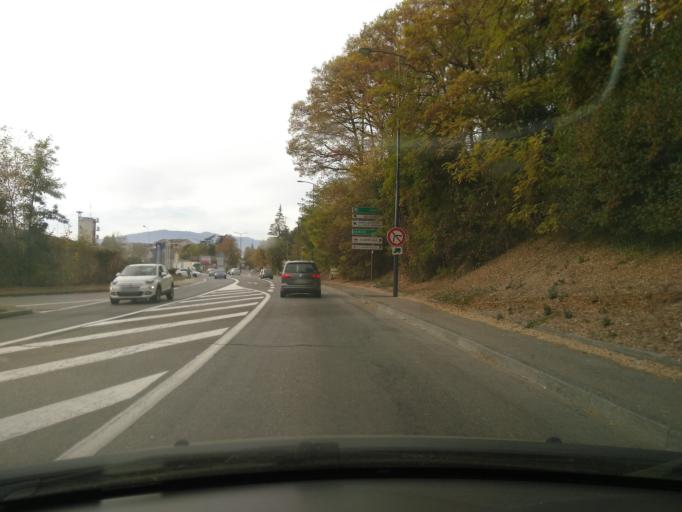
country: FR
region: Rhone-Alpes
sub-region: Departement de la Haute-Savoie
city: Saint-Julien-en-Genevois
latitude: 46.1431
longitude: 6.0901
